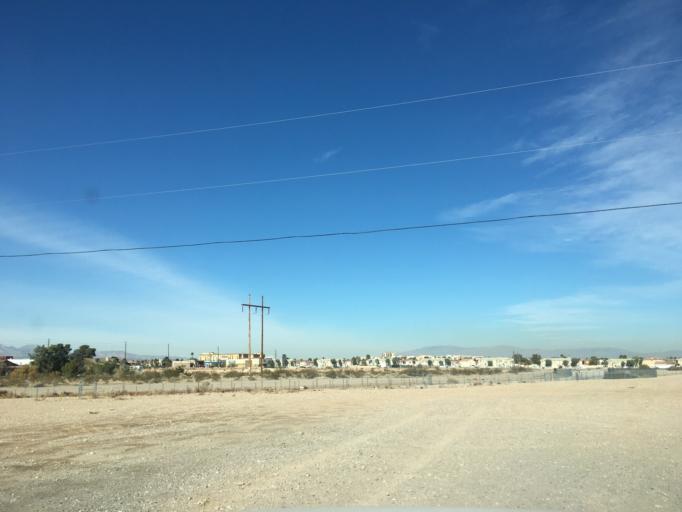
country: US
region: Nevada
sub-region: Clark County
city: Enterprise
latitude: 36.0090
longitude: -115.1679
